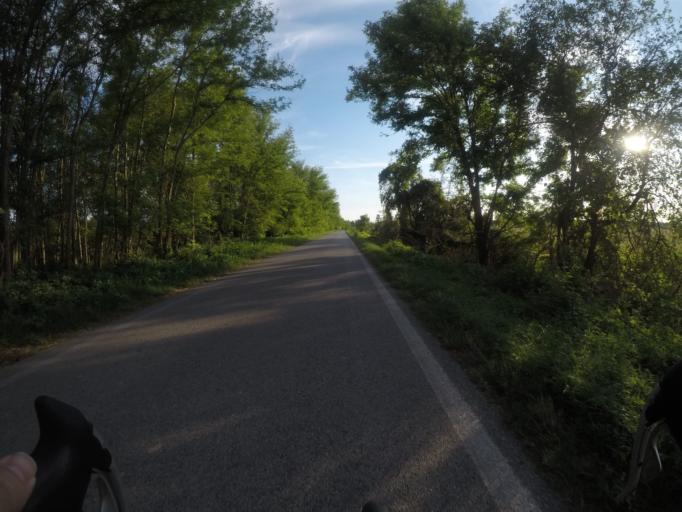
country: IT
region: Veneto
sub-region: Provincia di Rovigo
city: Pincara
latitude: 44.9971
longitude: 11.5986
